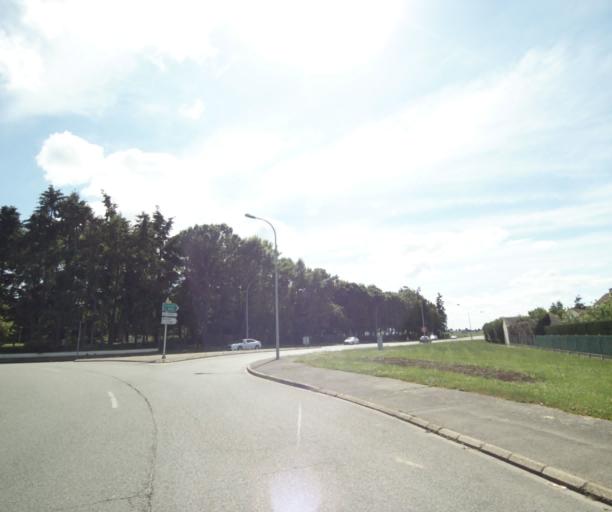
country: FR
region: Centre
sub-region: Departement d'Eure-et-Loir
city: Mainvilliers
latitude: 48.4370
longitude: 1.4426
